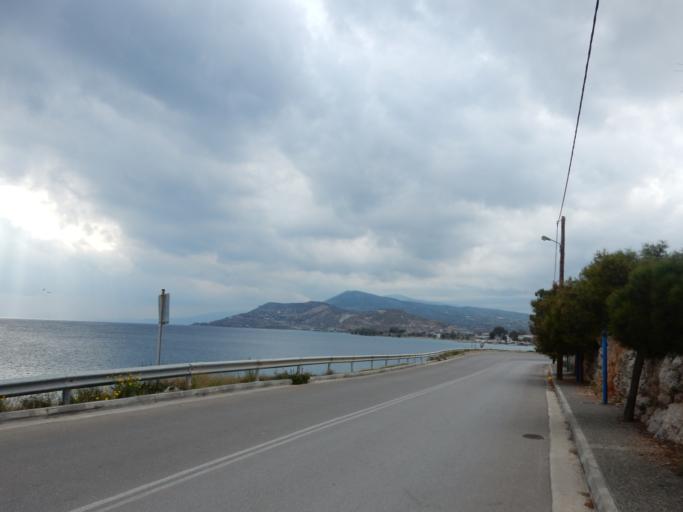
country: GR
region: Attica
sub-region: Nomarchia Dytikis Attikis
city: Megara
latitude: 37.9752
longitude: 23.3606
